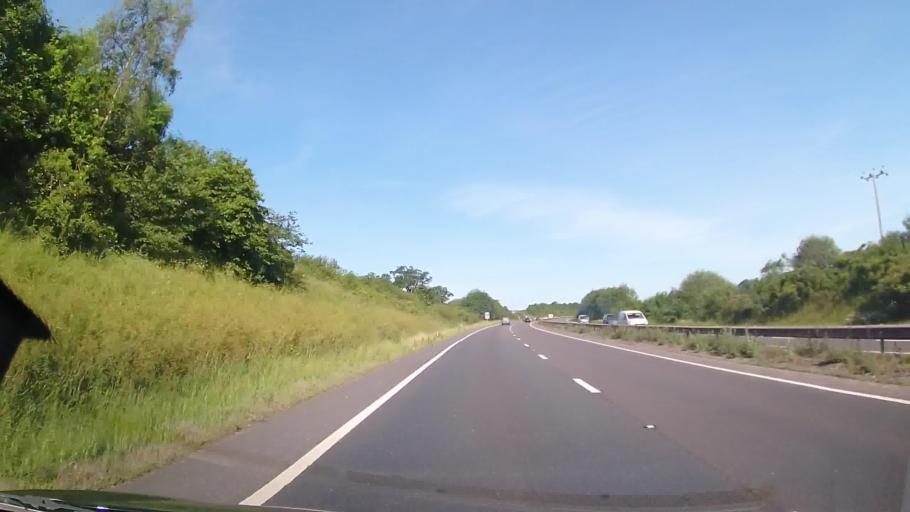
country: GB
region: England
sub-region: Shropshire
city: Bayston Hill
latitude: 52.6829
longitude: -2.7876
